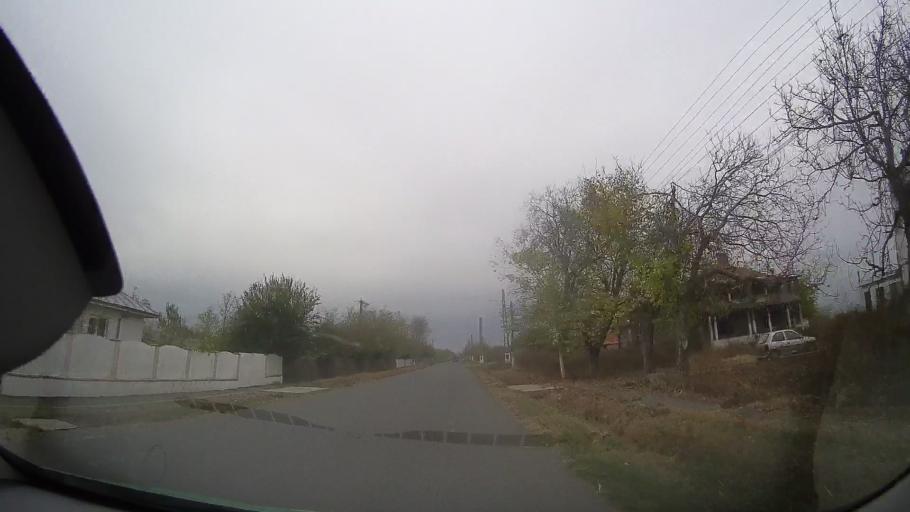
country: RO
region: Braila
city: Dudesti
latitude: 44.8754
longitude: 27.4305
